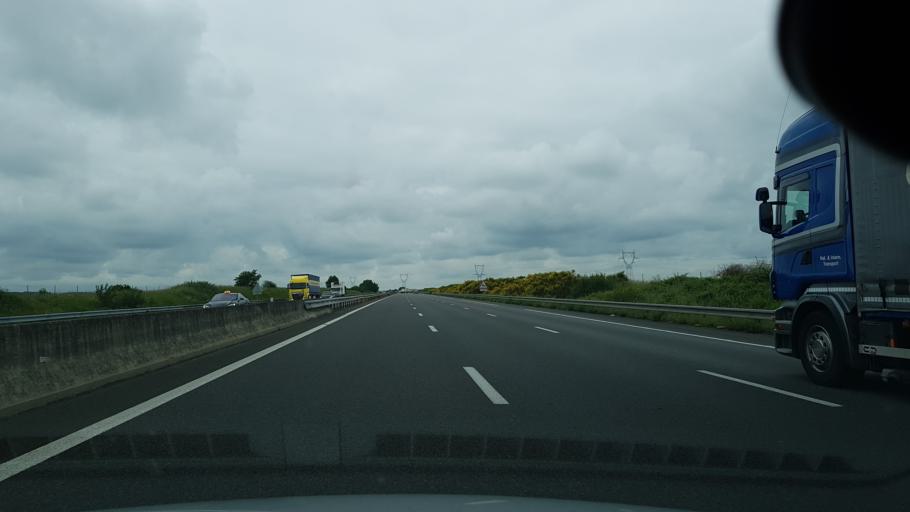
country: FR
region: Centre
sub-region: Departement du Loir-et-Cher
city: Herbault
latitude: 47.6164
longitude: 1.1947
